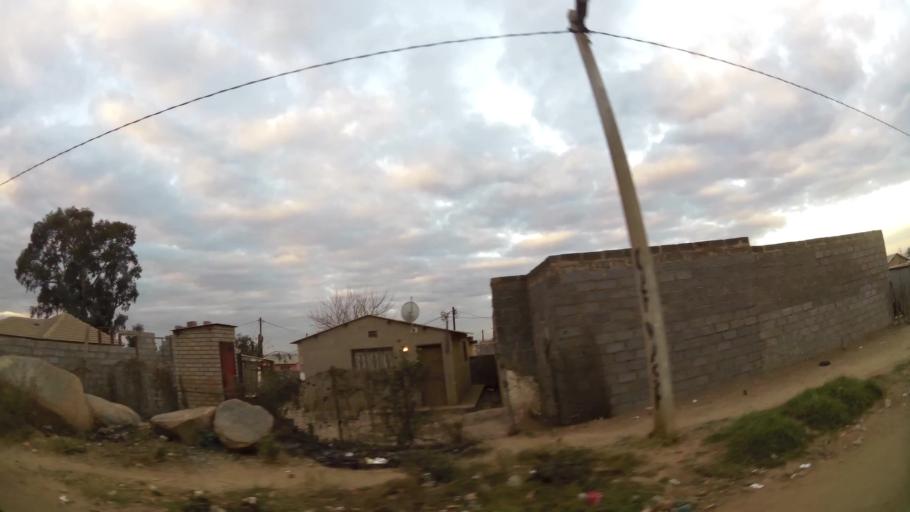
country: ZA
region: Gauteng
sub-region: City of Johannesburg Metropolitan Municipality
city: Midrand
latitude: -25.9811
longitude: 28.1730
